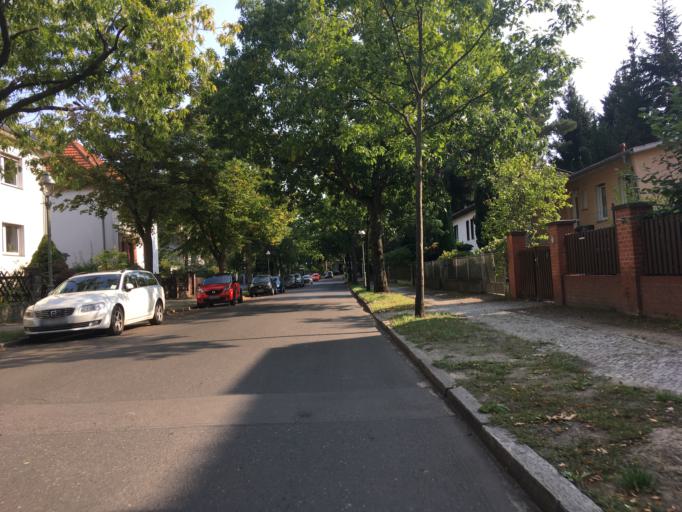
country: DE
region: Berlin
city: Hermsdorf
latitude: 52.6139
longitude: 13.3101
